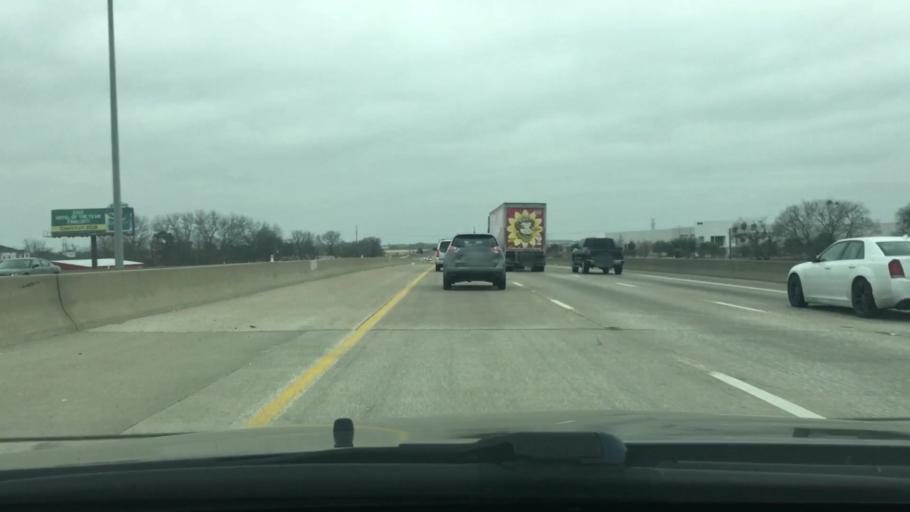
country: US
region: Texas
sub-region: Dallas County
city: Wilmer
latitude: 32.5910
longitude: -96.6791
